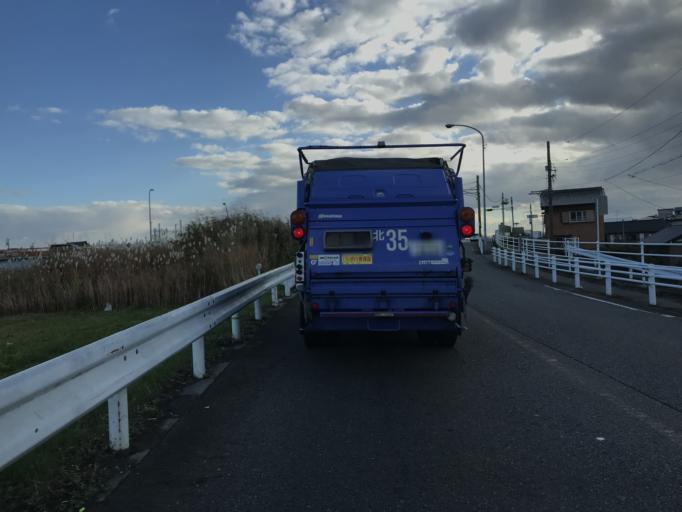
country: JP
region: Aichi
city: Nagoya-shi
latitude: 35.1868
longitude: 136.8444
